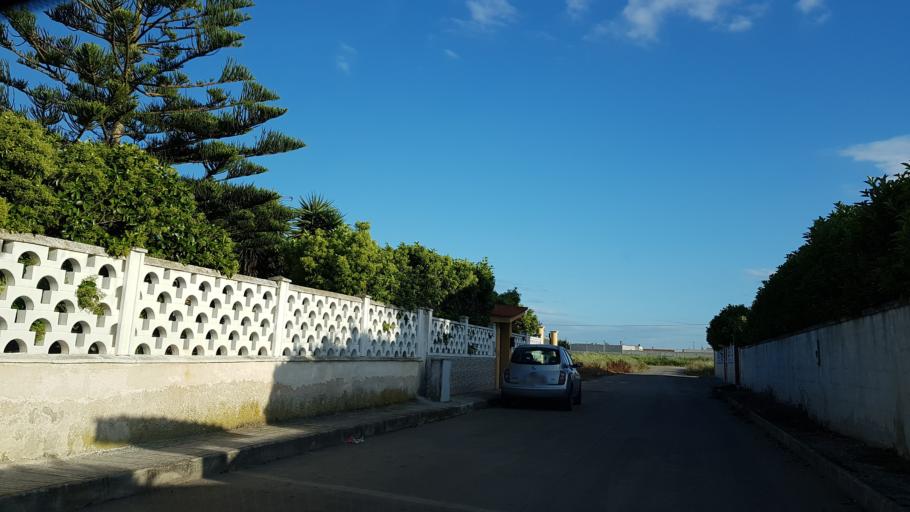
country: IT
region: Apulia
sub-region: Provincia di Brindisi
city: Brindisi
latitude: 40.6141
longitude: 17.9253
